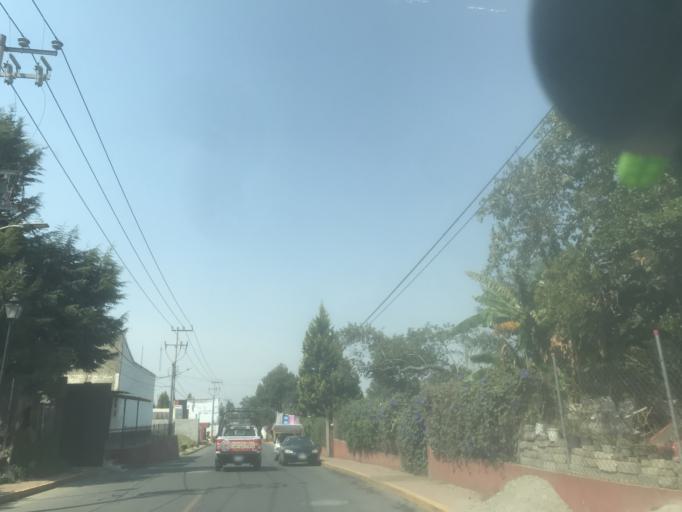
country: MX
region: Mexico
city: Ozumba de Alzate
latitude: 19.0310
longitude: -98.8001
